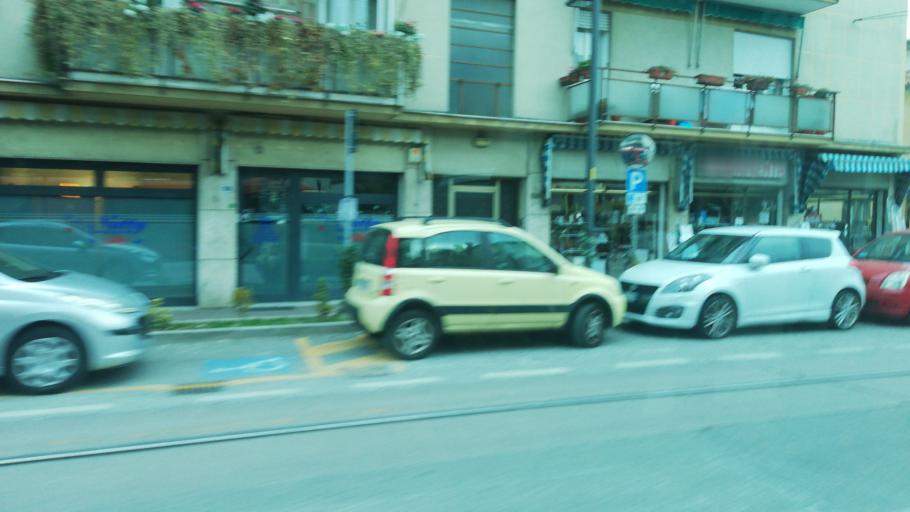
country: IT
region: Veneto
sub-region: Provincia di Venezia
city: Mestre
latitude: 45.5022
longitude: 12.2547
